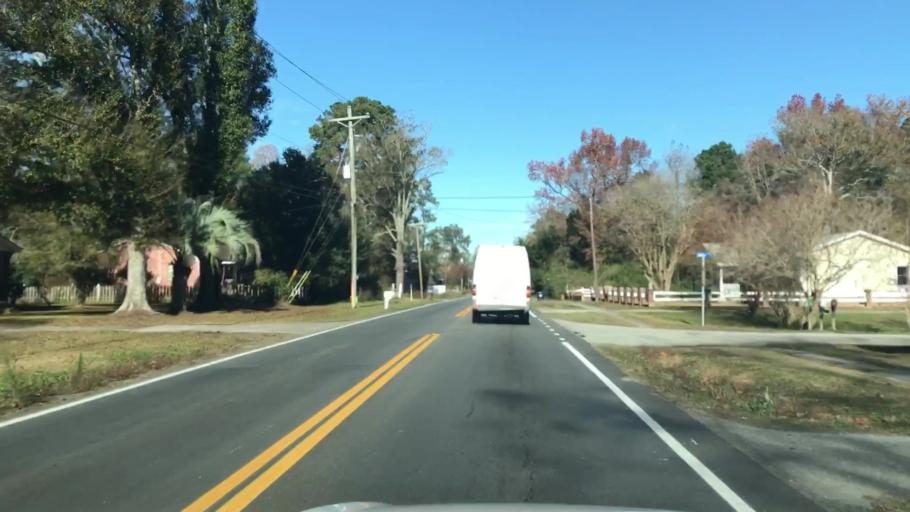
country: US
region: South Carolina
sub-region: Dorchester County
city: Summerville
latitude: 33.0047
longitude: -80.2343
